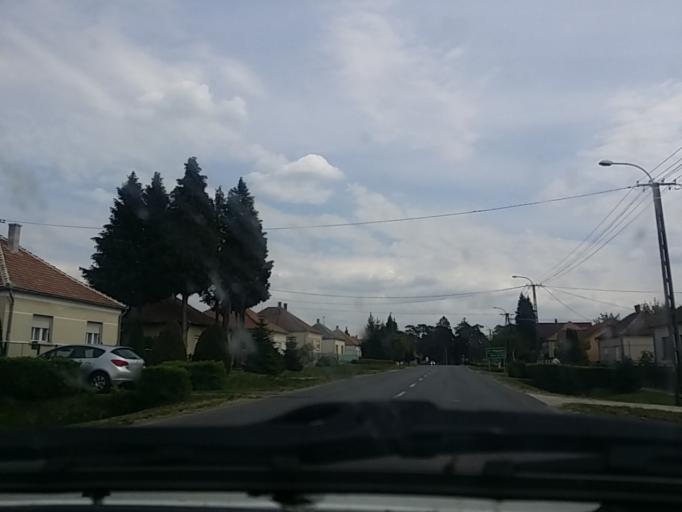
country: HU
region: Somogy
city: Berzence
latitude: 46.2054
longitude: 17.1590
